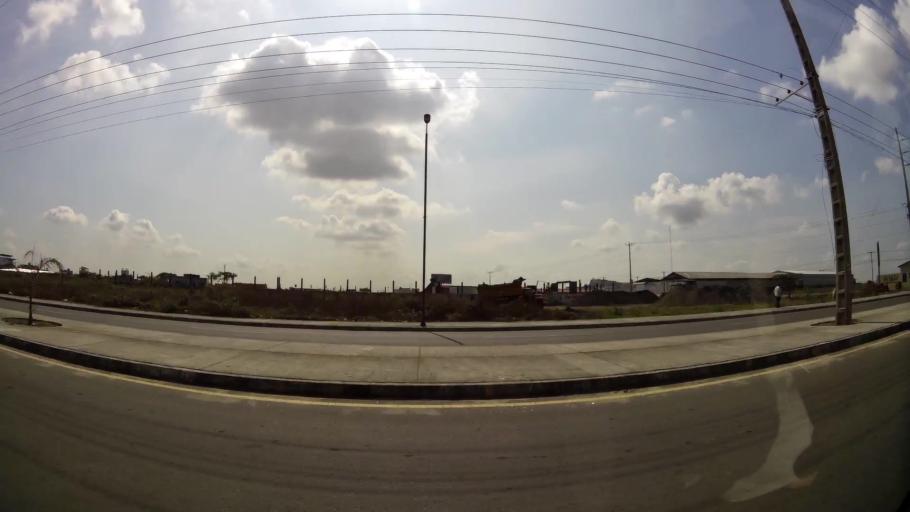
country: EC
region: Guayas
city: Eloy Alfaro
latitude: -2.1773
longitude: -79.8033
